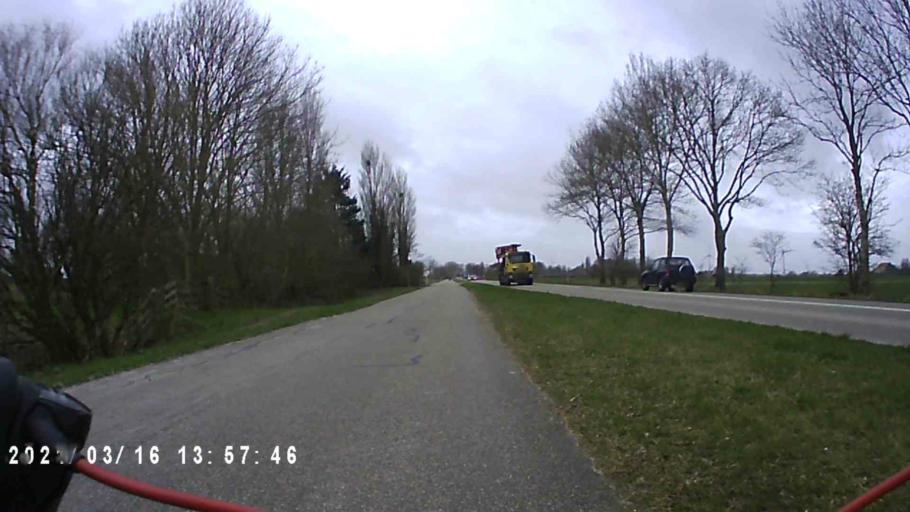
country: NL
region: Friesland
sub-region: Gemeente Franekeradeel
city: Franeker
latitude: 53.1838
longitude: 5.5054
